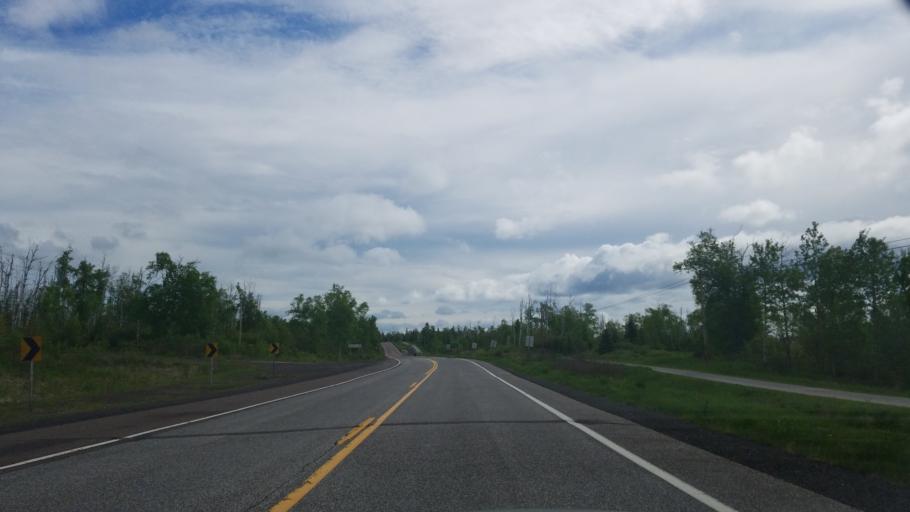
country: US
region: Minnesota
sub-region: Lake County
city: Silver Bay
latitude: 47.1515
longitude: -91.4487
